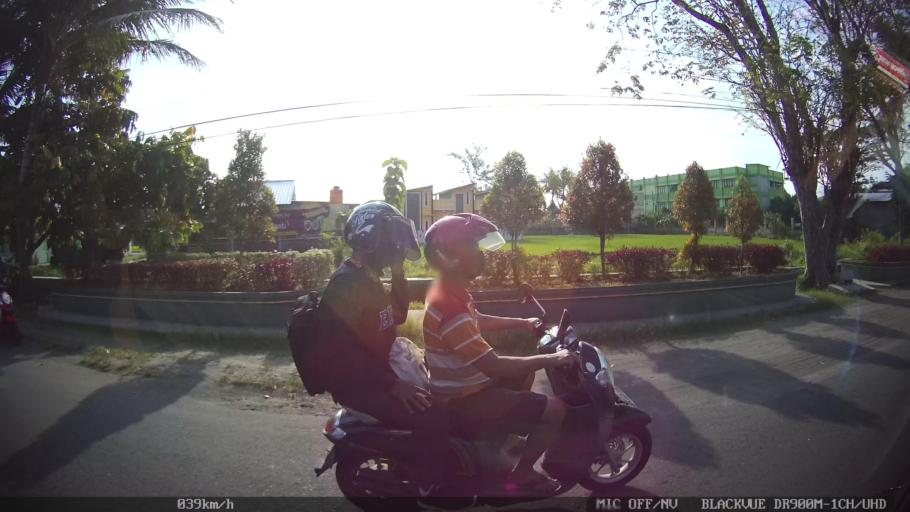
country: ID
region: Daerah Istimewa Yogyakarta
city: Bantul
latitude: -7.8966
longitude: 110.3234
